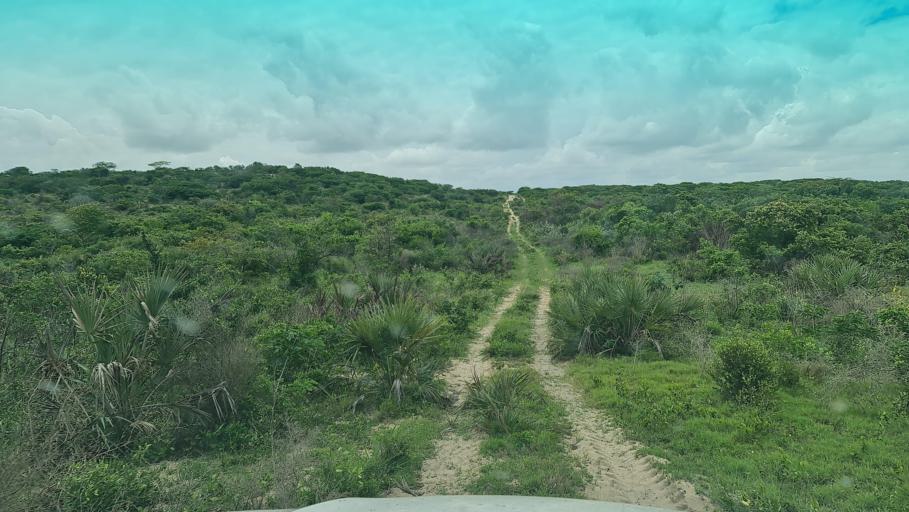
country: MZ
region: Maputo
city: Manhica
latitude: -25.6276
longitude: 32.7873
